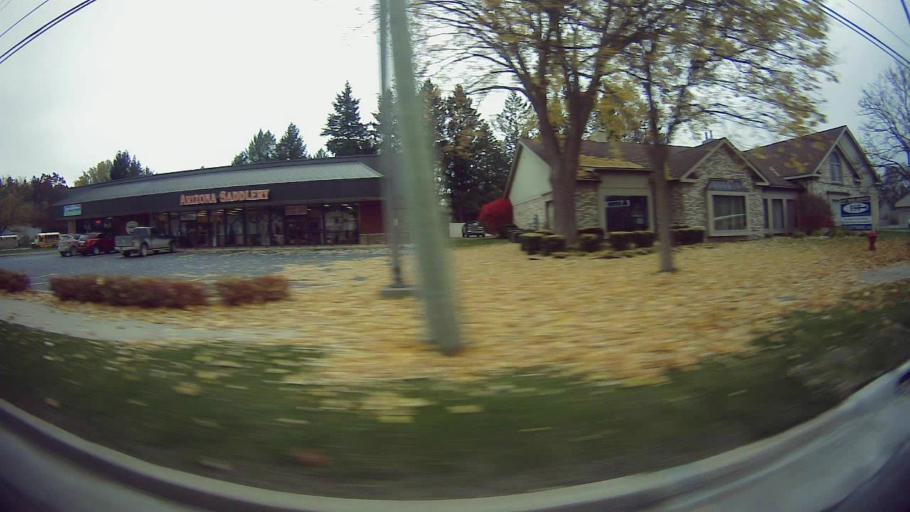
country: US
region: Michigan
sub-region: Oakland County
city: Waterford
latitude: 42.7150
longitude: -83.4120
